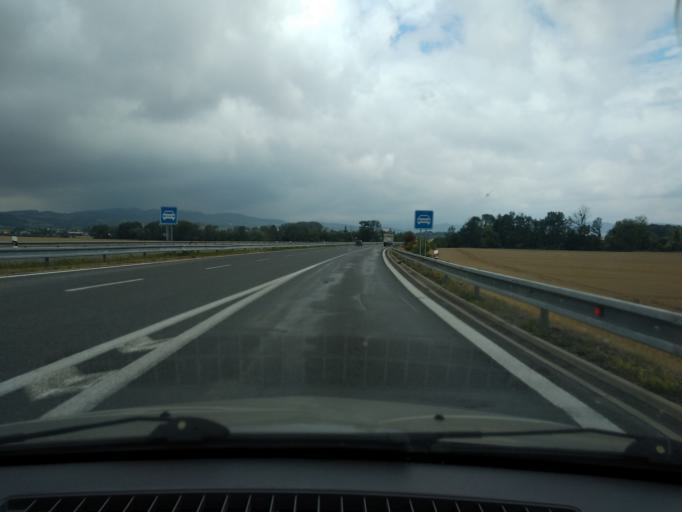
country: CZ
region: Olomoucky
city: Postrelmov
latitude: 49.8952
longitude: 16.8948
